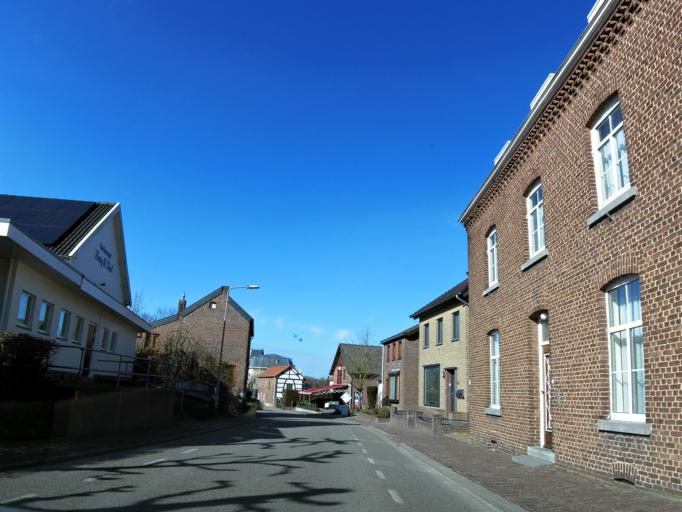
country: BE
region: Flanders
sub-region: Provincie Limburg
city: Sint-Pieters-Voeren
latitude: 50.7692
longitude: 5.8608
